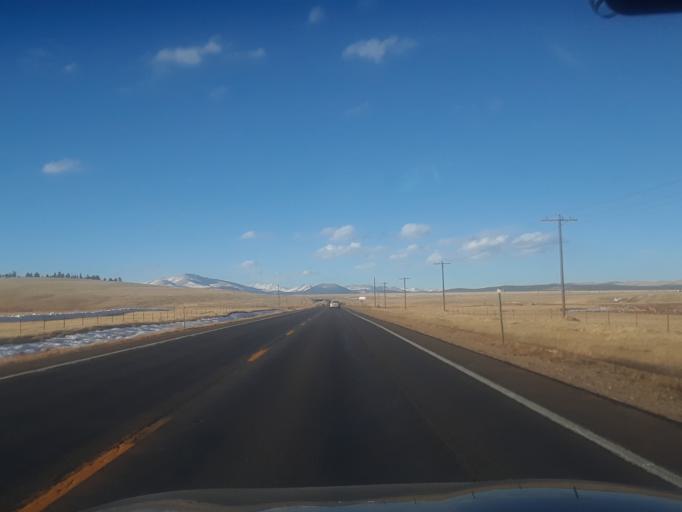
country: US
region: Colorado
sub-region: Park County
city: Fairplay
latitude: 39.0642
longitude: -105.9751
